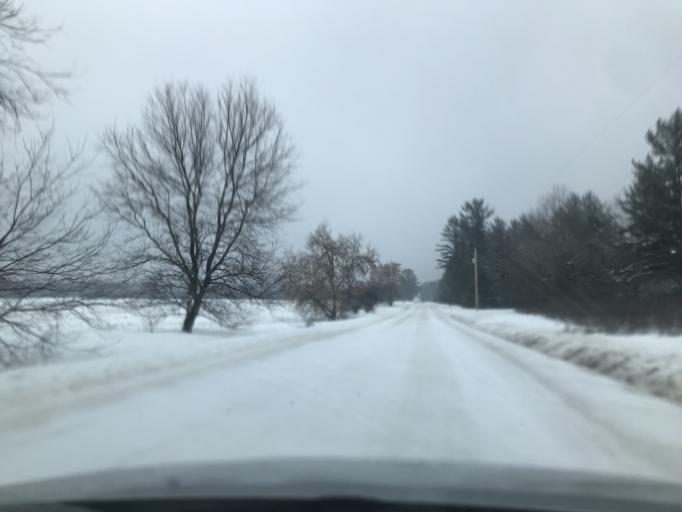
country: US
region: Wisconsin
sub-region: Marinette County
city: Peshtigo
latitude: 45.3813
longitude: -87.9417
